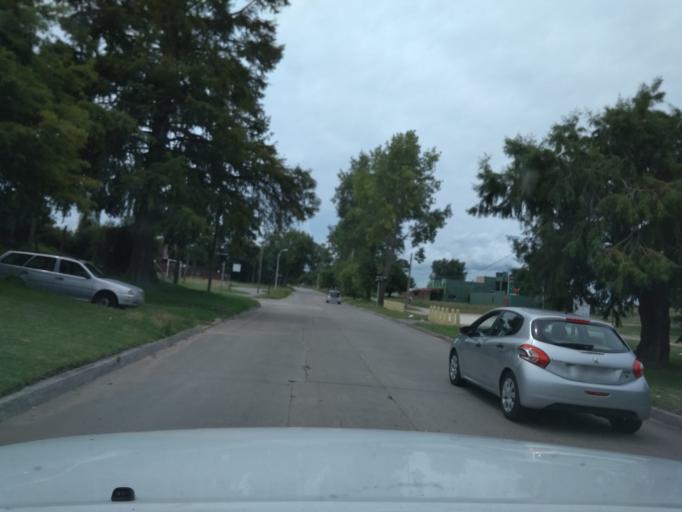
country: UY
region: Canelones
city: Paso de Carrasco
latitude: -34.8736
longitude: -56.0584
